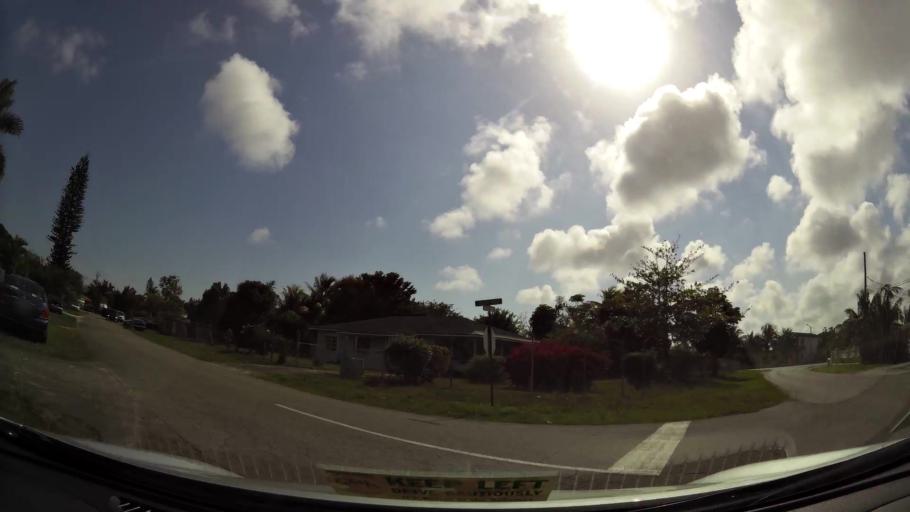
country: BS
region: Freeport
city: Freeport
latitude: 26.5284
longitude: -78.6845
